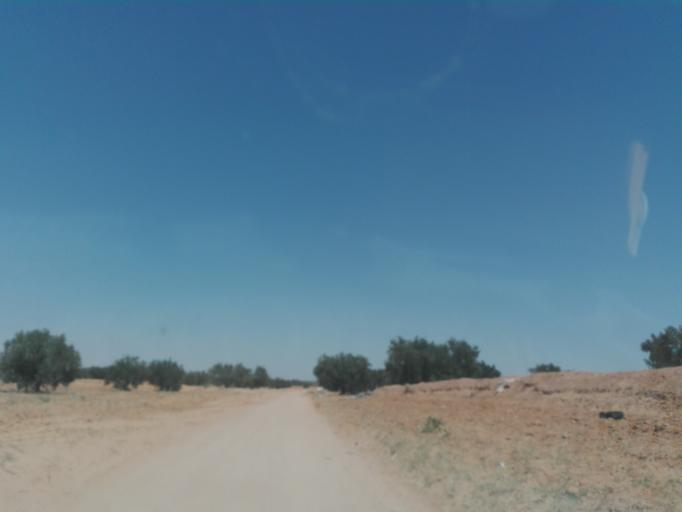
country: TN
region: Safaqis
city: Bi'r `Ali Bin Khalifah
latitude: 34.6727
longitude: 10.2316
